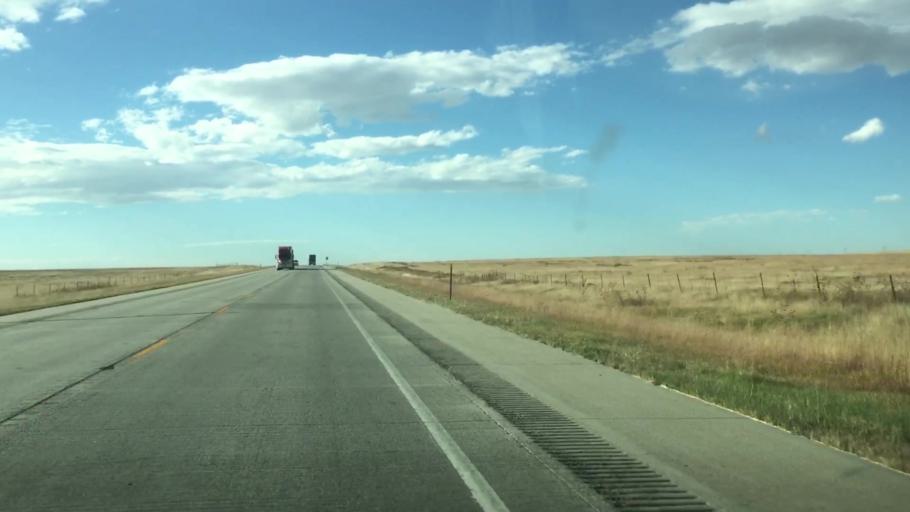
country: US
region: Colorado
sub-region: Lincoln County
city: Hugo
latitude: 39.1848
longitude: -103.5524
